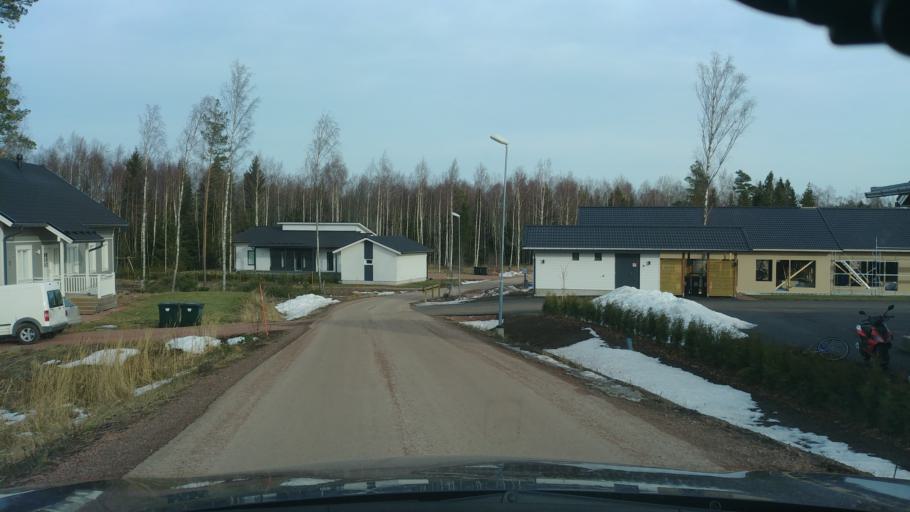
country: AX
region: Mariehamns stad
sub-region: Mariehamn
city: Mariehamn
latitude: 60.1003
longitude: 19.8953
